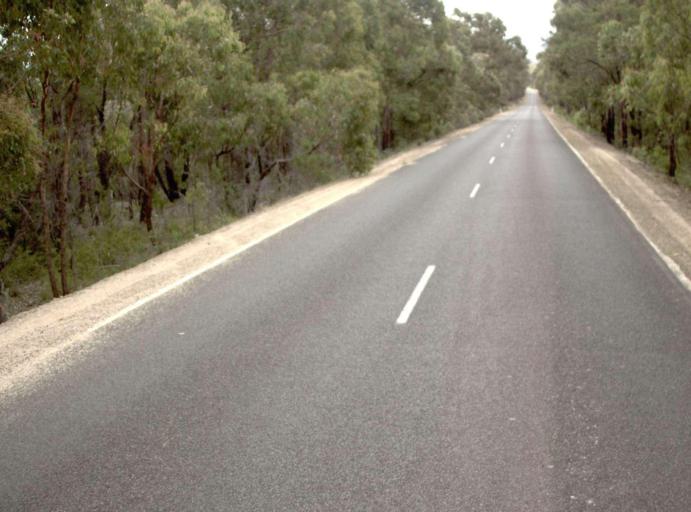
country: AU
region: Victoria
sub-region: Latrobe
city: Traralgon
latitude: -38.3953
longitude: 146.8131
